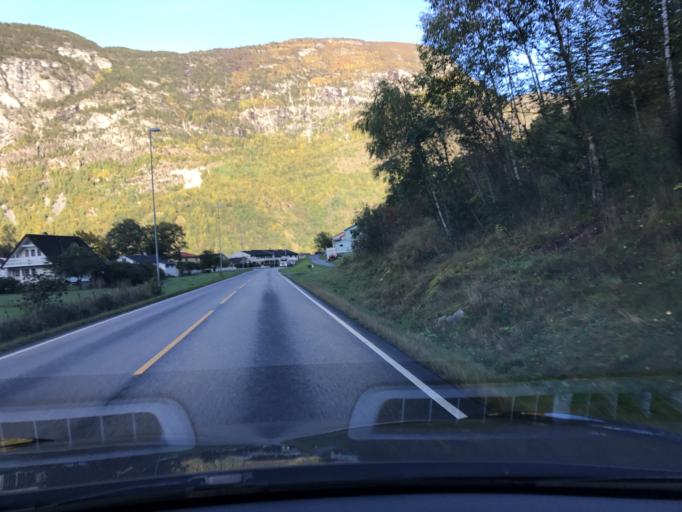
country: NO
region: Sogn og Fjordane
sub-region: Laerdal
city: Laerdalsoyri
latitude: 61.0988
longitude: 7.4985
